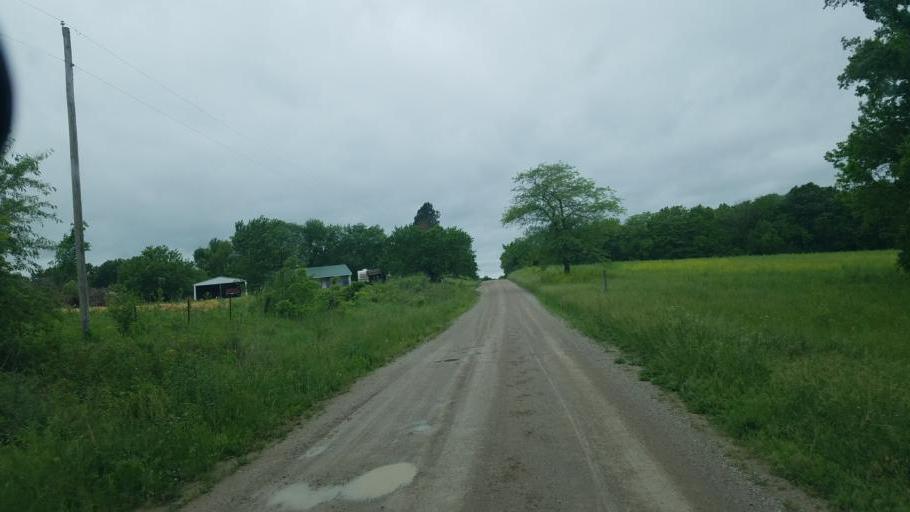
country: US
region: Missouri
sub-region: Carroll County
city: Carrollton
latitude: 39.4852
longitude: -93.5079
